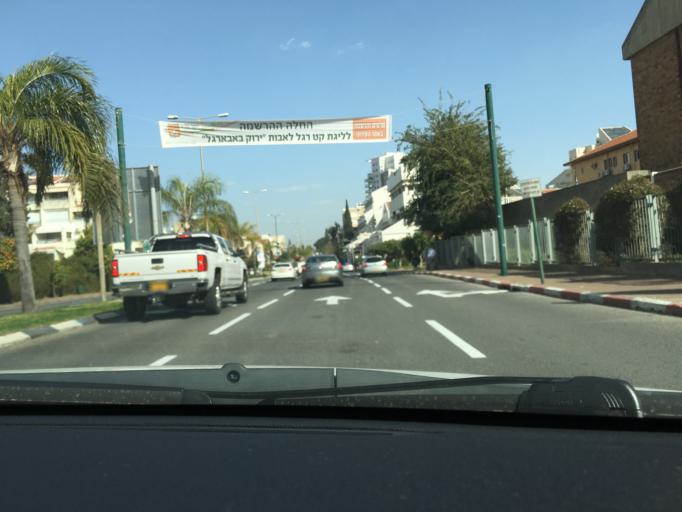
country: IL
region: Central District
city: Kfar Saba
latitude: 32.1760
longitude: 34.8923
